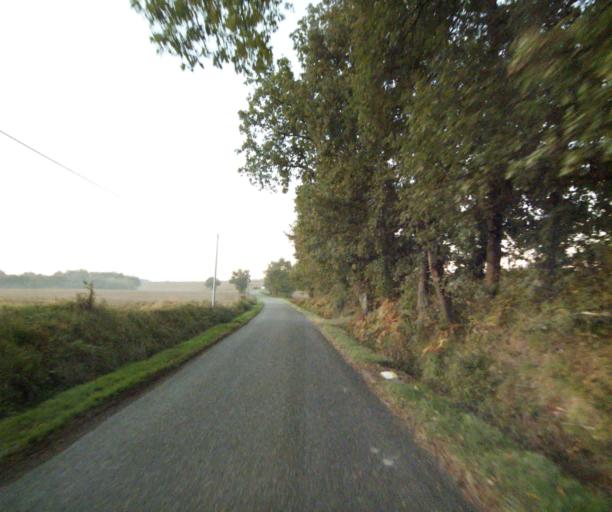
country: FR
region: Midi-Pyrenees
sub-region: Departement du Gers
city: Vic-Fezensac
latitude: 43.7829
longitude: 0.2224
